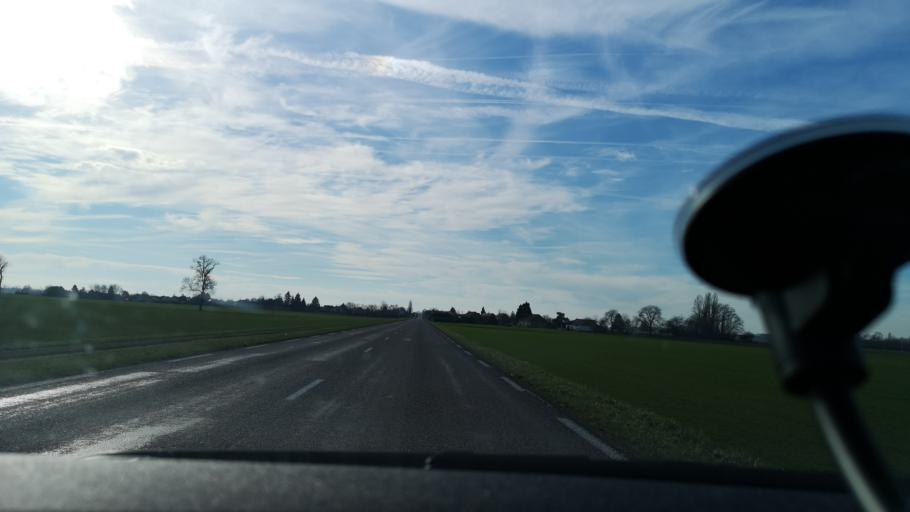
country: FR
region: Franche-Comte
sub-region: Departement du Jura
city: Petit-Noir
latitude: 46.9729
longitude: 5.3055
